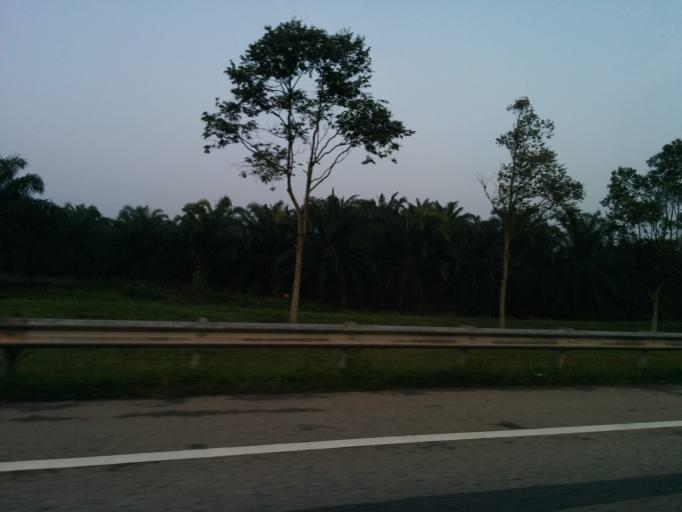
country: MY
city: Sungai Pelek New Village
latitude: 2.7616
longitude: 101.6860
